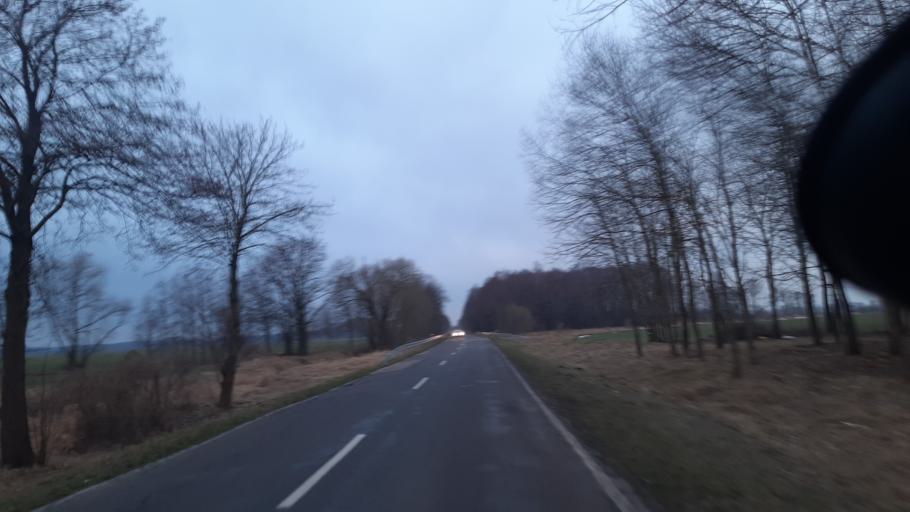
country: PL
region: Lublin Voivodeship
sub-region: Powiat parczewski
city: Sosnowica
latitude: 51.6169
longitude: 23.1066
